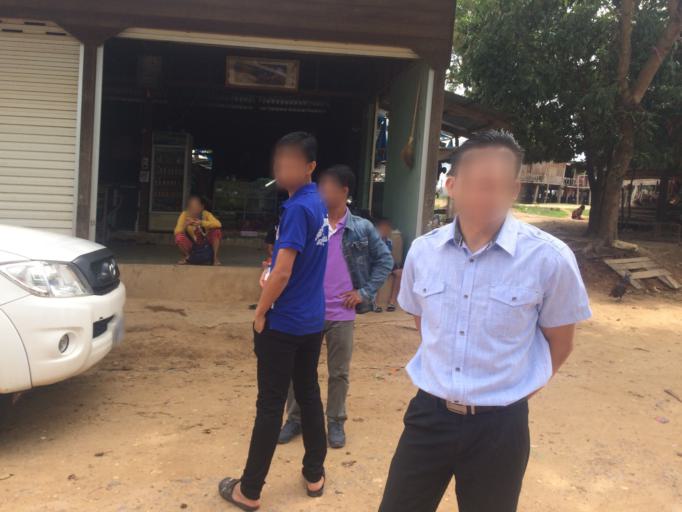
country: VN
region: Quang Tri
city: Khe Sanh
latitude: 16.6035
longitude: 106.4215
